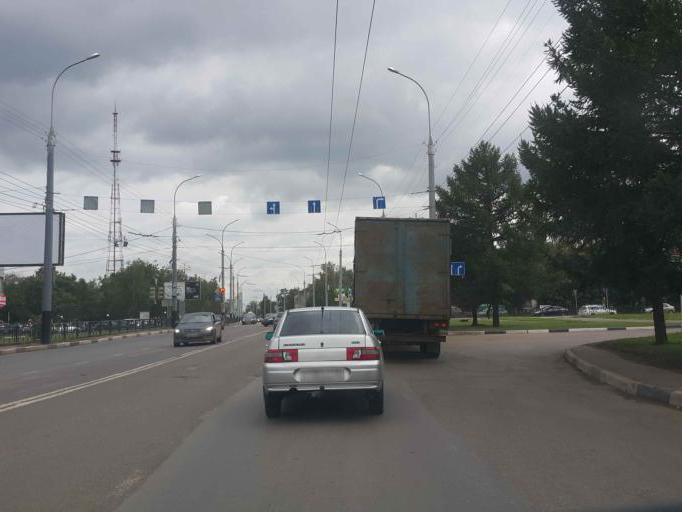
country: RU
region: Tambov
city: Tambov
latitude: 52.7480
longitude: 41.4191
